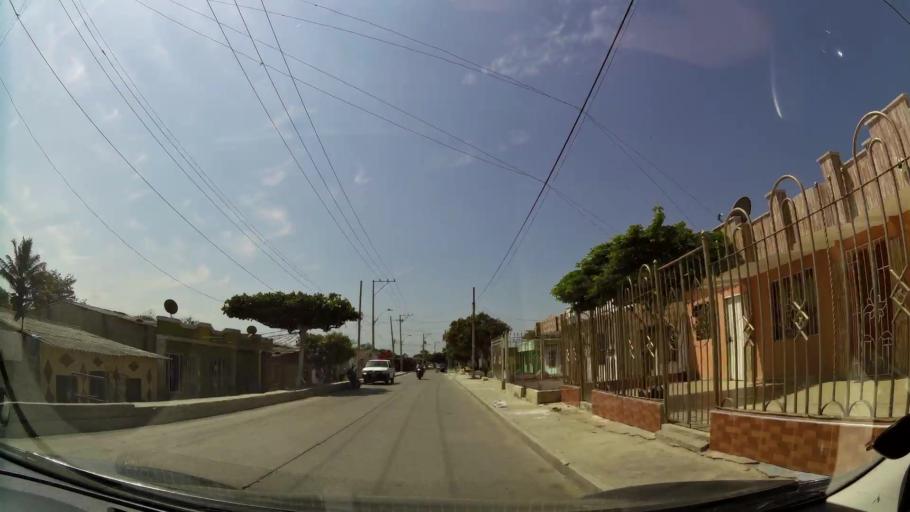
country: CO
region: Atlantico
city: Barranquilla
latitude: 10.9639
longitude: -74.8171
